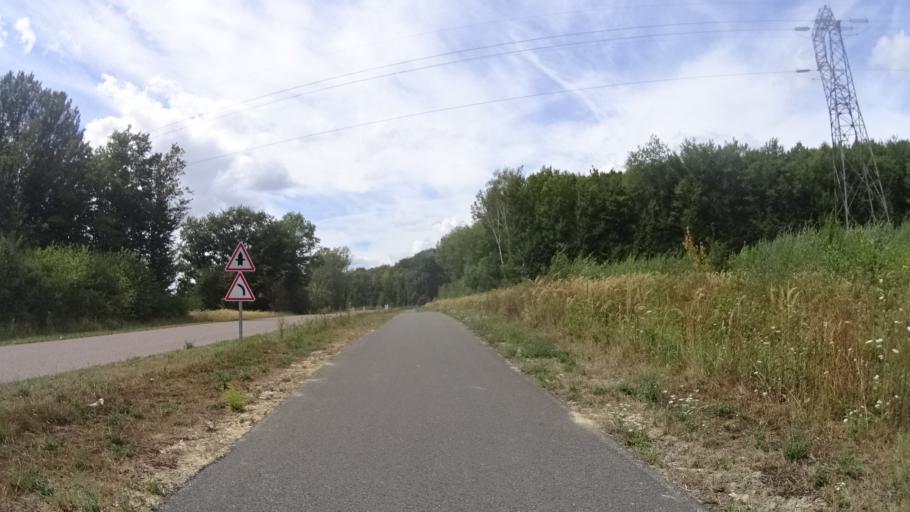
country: FR
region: Franche-Comte
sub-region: Departement du Jura
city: Damparis
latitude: 47.0773
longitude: 5.3937
